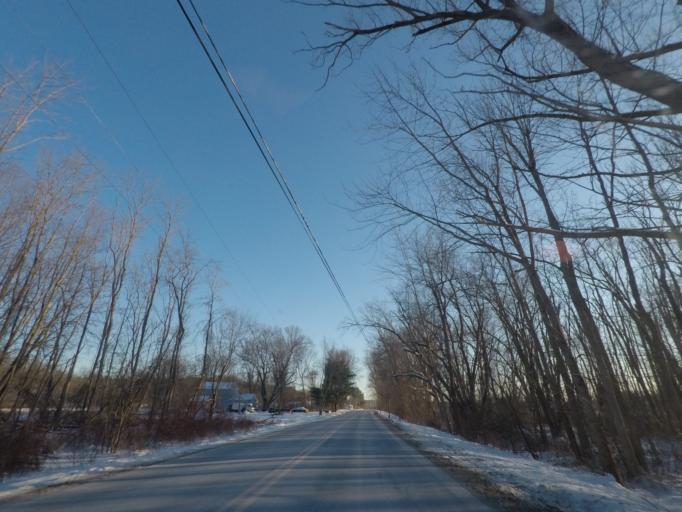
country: US
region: New York
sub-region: Saratoga County
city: Waterford
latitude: 42.8381
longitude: -73.6658
